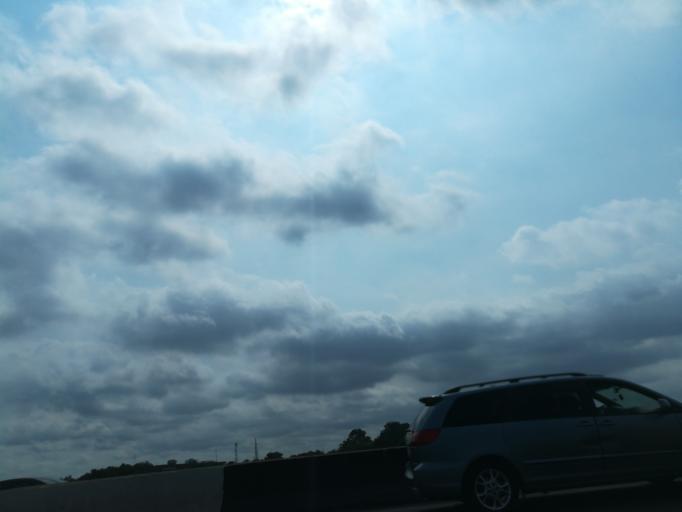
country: NG
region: Lagos
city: Makoko
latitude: 6.5178
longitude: 3.4056
